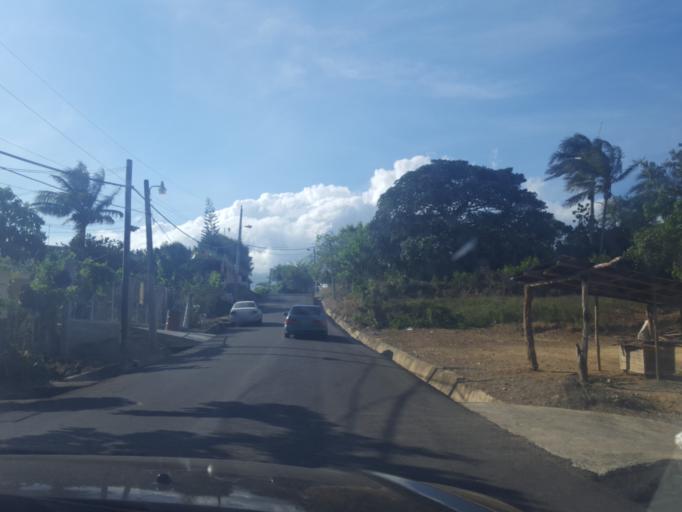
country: DO
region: La Vega
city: Rio Verde Arriba
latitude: 19.3494
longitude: -70.6261
